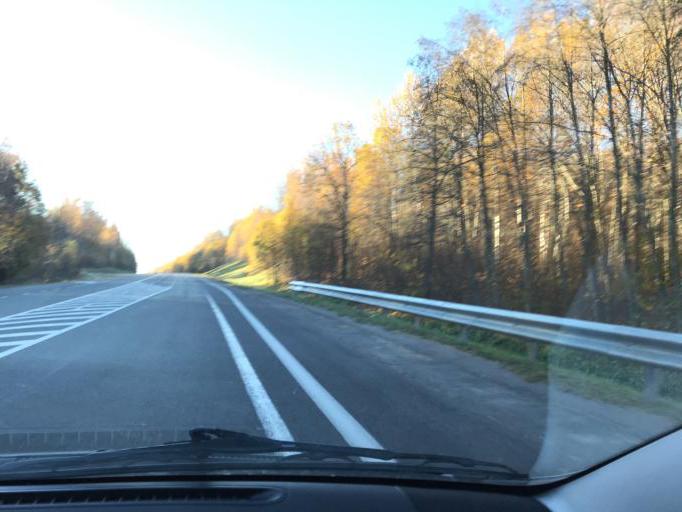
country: BY
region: Vitebsk
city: Vitebsk
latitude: 55.0258
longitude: 30.3242
